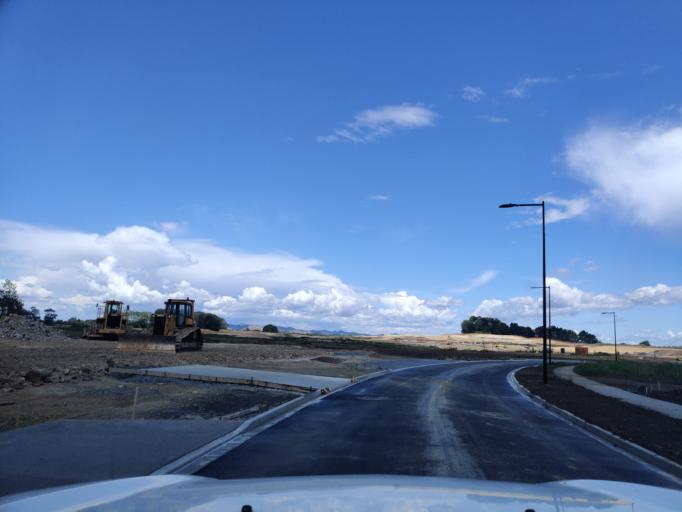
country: NZ
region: Waikato
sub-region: Waikato District
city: Te Kauwhata
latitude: -37.4105
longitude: 175.1532
